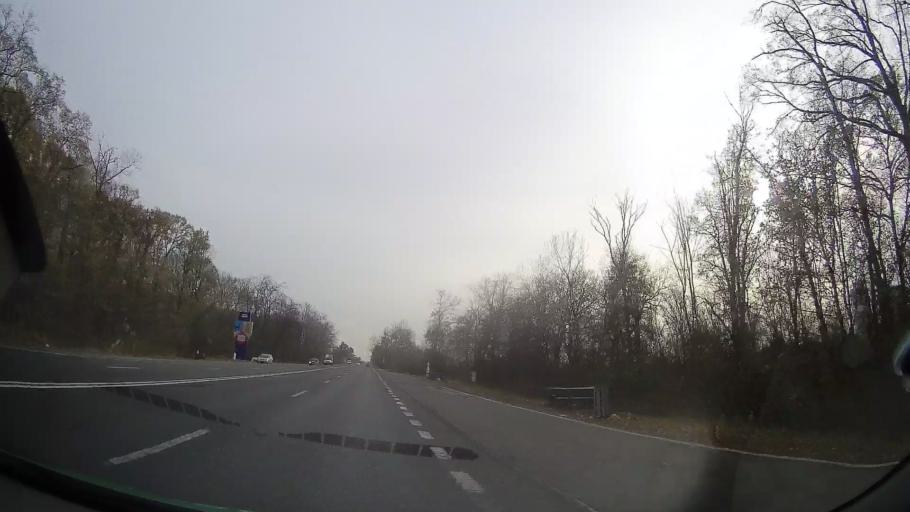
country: RO
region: Prahova
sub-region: Comuna Gorgota
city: Potigrafu
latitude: 44.7669
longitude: 26.1031
